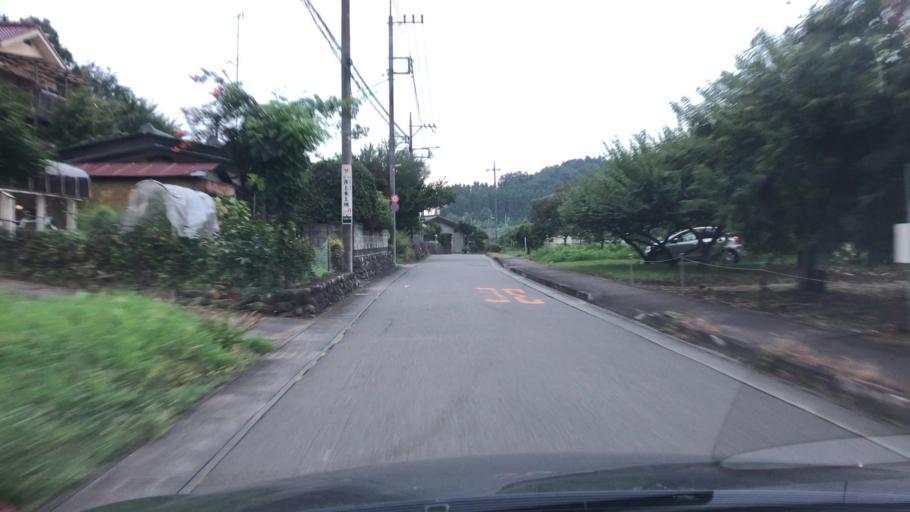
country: JP
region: Tokyo
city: Itsukaichi
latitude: 35.7451
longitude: 139.2480
